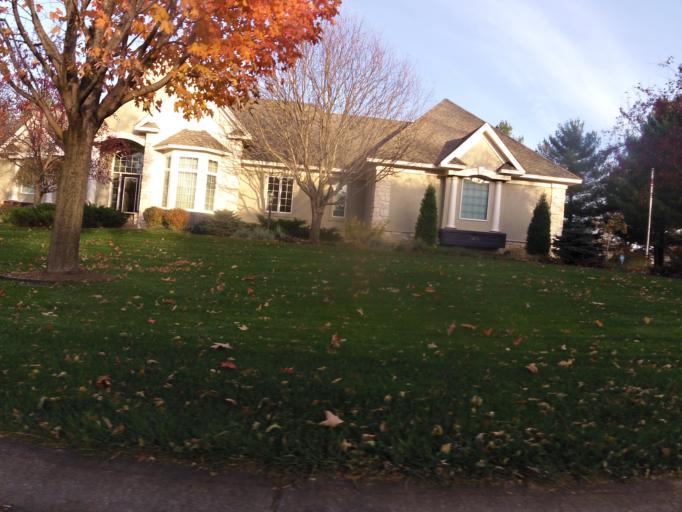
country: US
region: Minnesota
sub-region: Washington County
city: Lake Elmo
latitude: 44.9692
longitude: -92.8789
